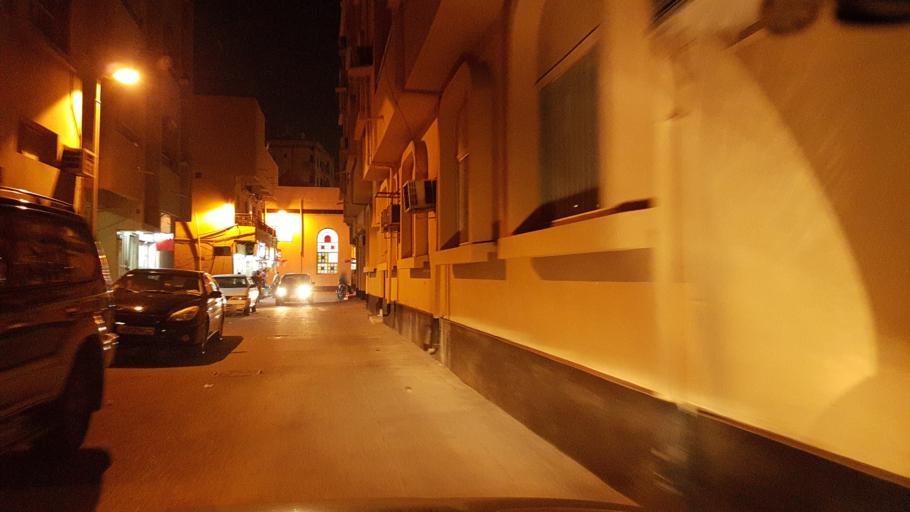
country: BH
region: Manama
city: Manama
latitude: 26.2169
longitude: 50.5862
